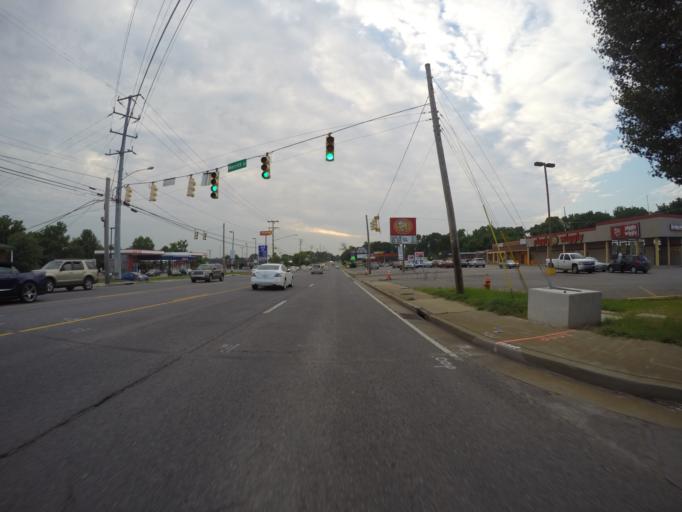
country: US
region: Tennessee
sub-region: Davidson County
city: Lakewood
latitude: 36.2556
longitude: -86.6536
